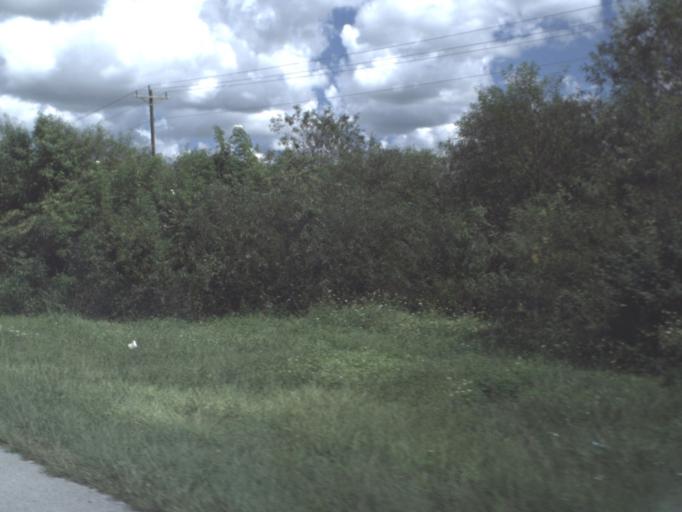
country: US
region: Florida
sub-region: Collier County
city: Immokalee
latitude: 26.4797
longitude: -81.4345
